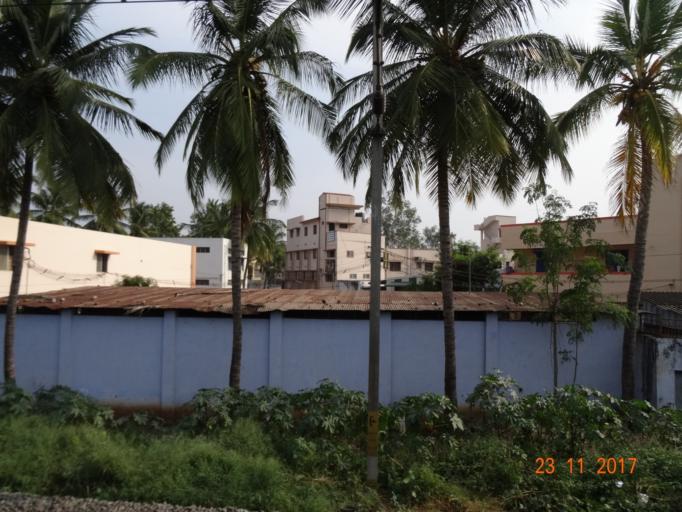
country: IN
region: Tamil Nadu
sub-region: Coimbatore
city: Coimbatore
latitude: 11.0275
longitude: 76.9760
